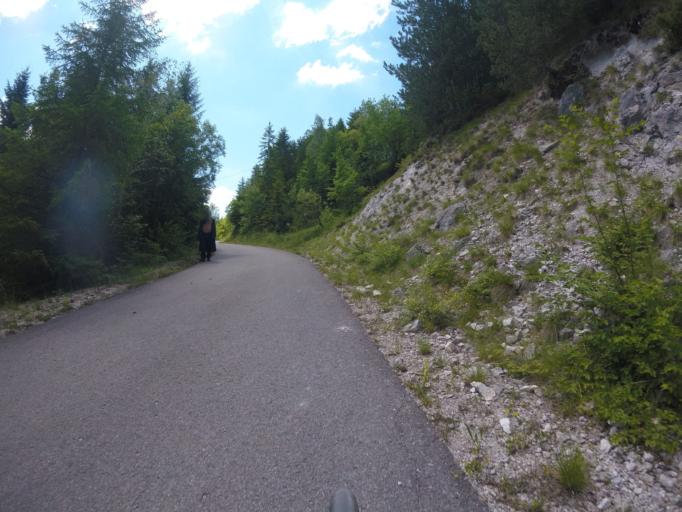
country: SI
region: Kostanjevica na Krki
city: Kostanjevica na Krki
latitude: 45.7615
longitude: 15.3968
